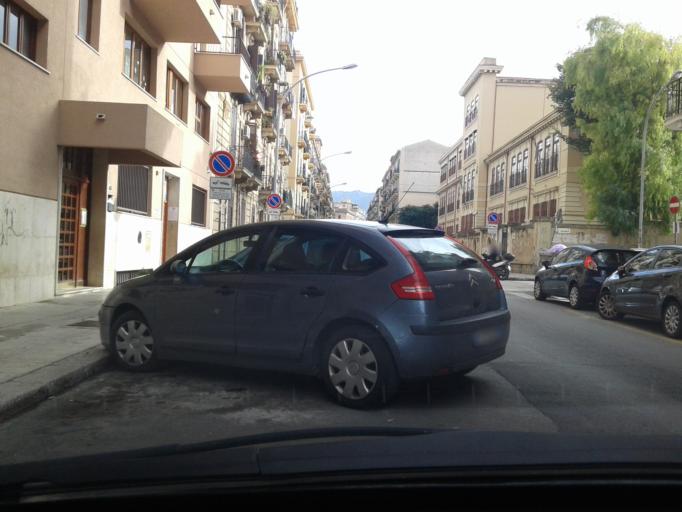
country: IT
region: Sicily
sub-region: Palermo
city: Palermo
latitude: 38.1207
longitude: 13.3444
